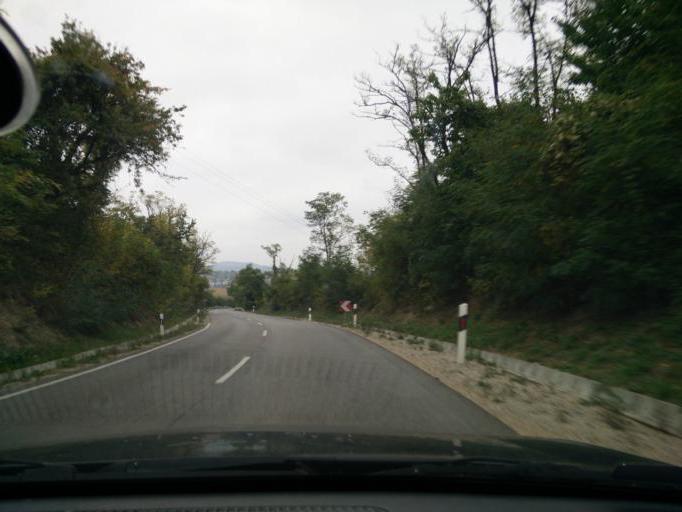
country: HU
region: Komarom-Esztergom
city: Bajna
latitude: 47.6721
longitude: 18.6049
